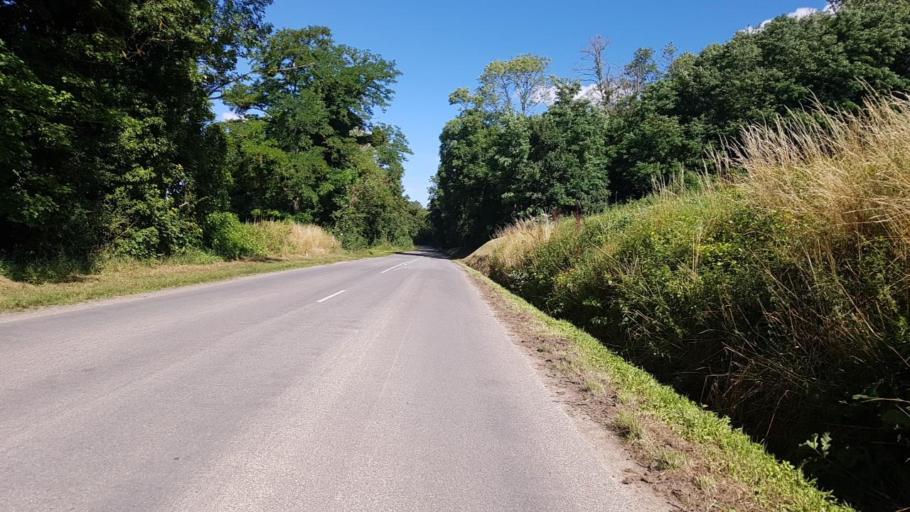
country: FR
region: Picardie
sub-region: Departement de l'Aisne
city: Charly-sur-Marne
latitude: 48.9728
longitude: 3.2535
